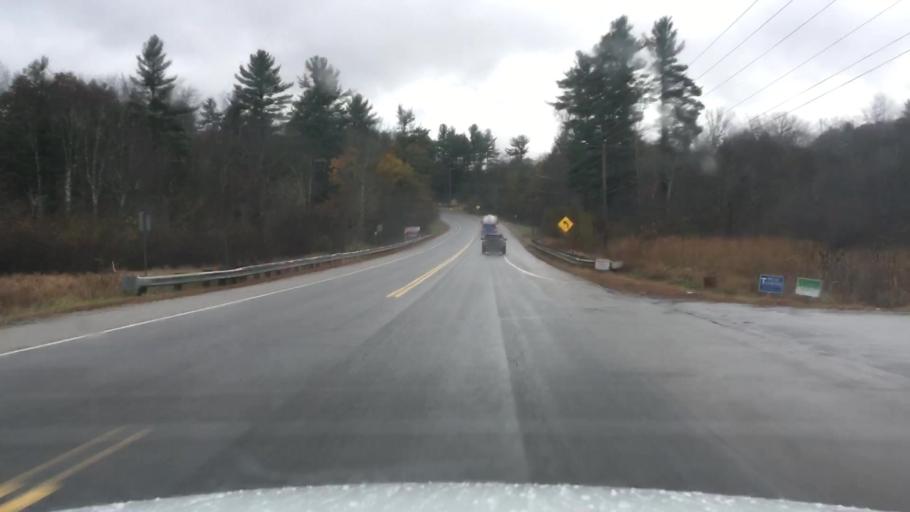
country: US
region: New Hampshire
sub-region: Strafford County
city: Barrington
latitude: 43.2340
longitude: -70.9920
